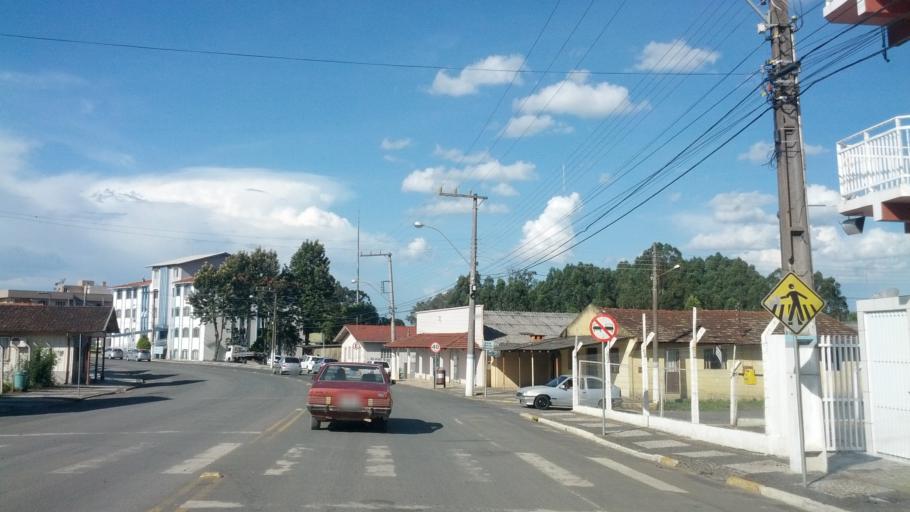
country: BR
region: Santa Catarina
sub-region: Otacilio Costa
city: Otacilio Costa
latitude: -27.4840
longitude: -50.1196
